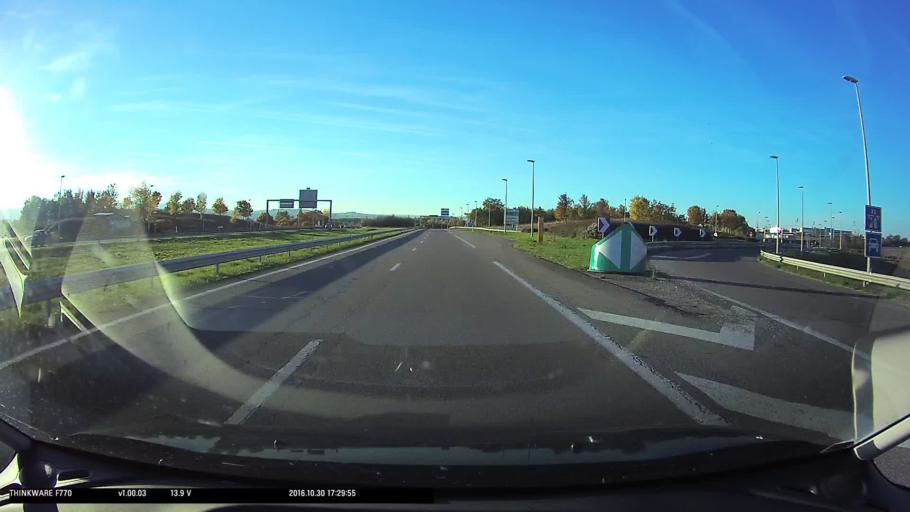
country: FR
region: Bourgogne
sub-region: Departement de la Cote-d'Or
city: Longvic
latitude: 47.3022
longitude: 5.0793
